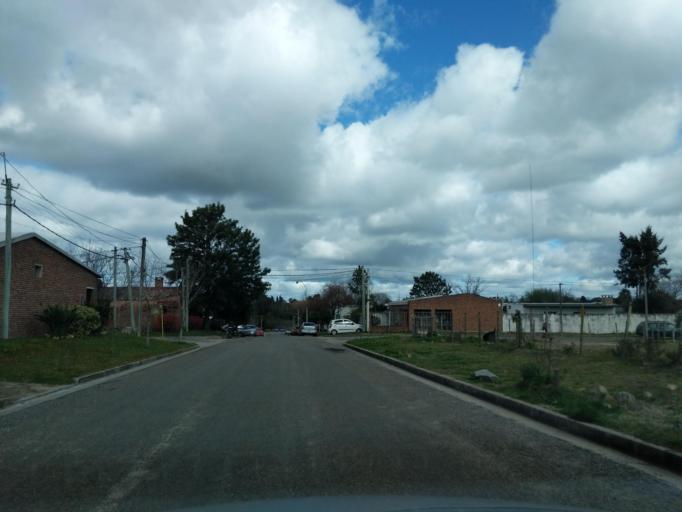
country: UY
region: Florida
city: Florida
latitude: -34.0908
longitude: -56.2324
